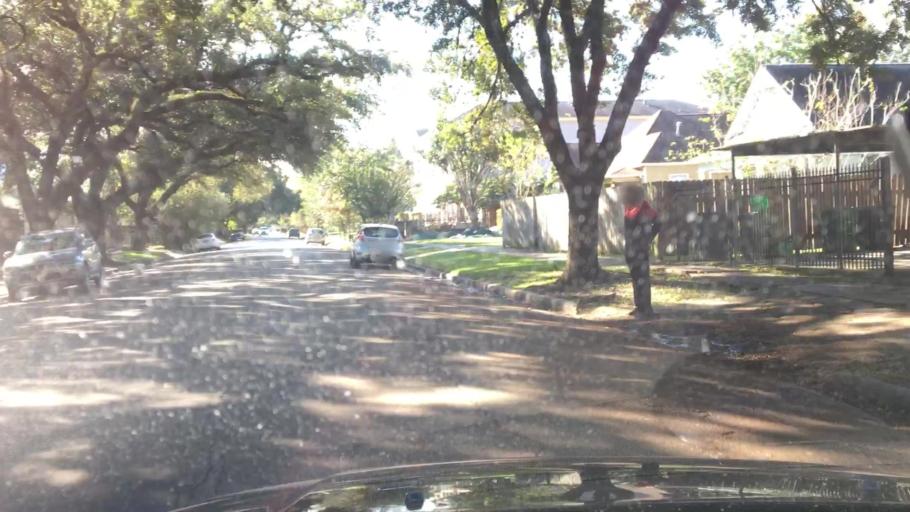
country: US
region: Texas
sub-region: Harris County
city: Houston
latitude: 29.7989
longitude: -95.4014
